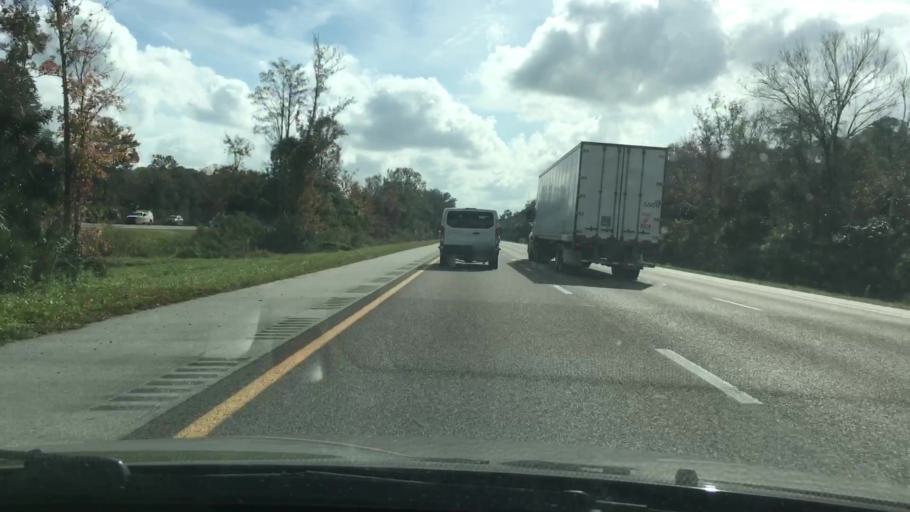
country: US
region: Florida
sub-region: Volusia County
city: Oak Hill
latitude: 28.8656
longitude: -80.9190
